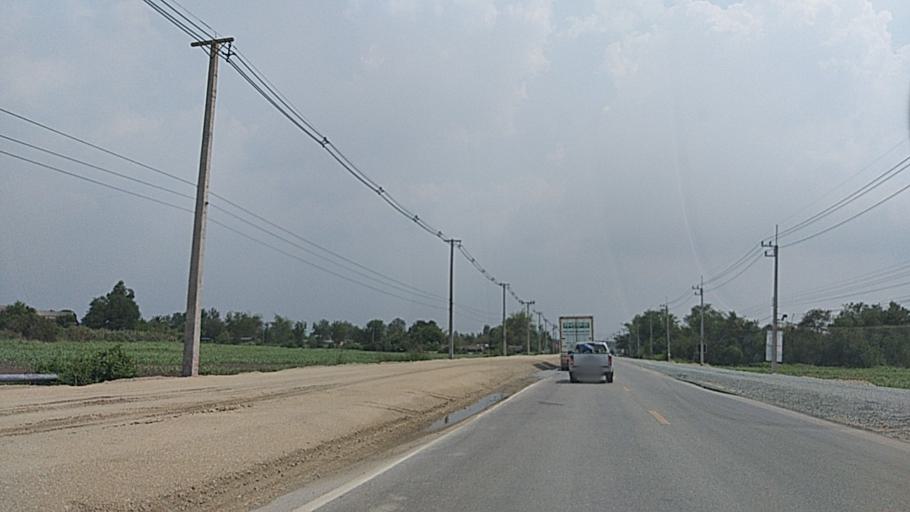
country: TH
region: Chon Buri
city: Phanat Nikhom
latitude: 13.3711
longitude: 101.1954
